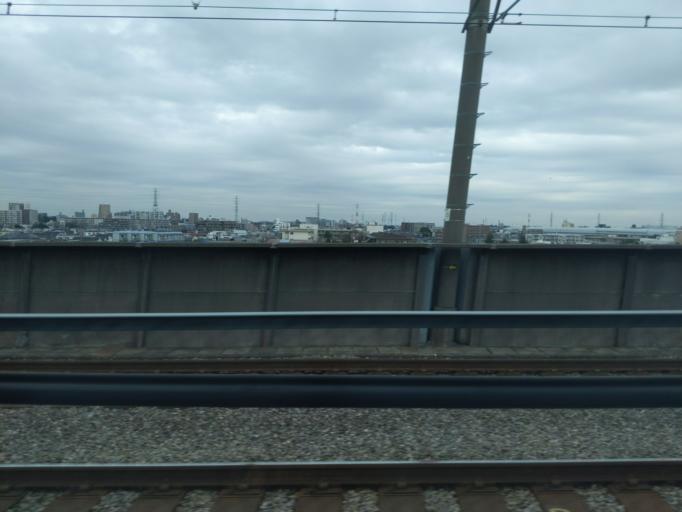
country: JP
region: Saitama
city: Shimotoda
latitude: 35.8335
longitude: 139.6539
